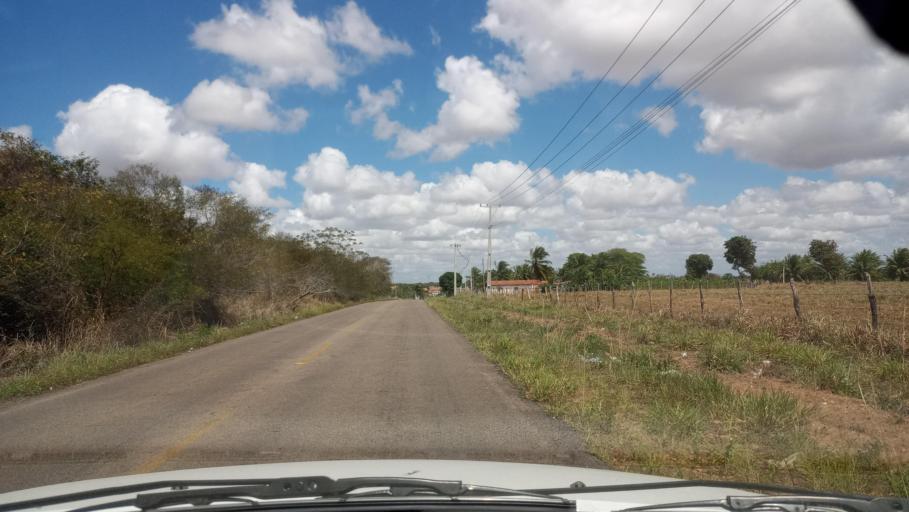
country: BR
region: Rio Grande do Norte
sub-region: Brejinho
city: Brejinho
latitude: -6.0413
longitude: -35.4200
